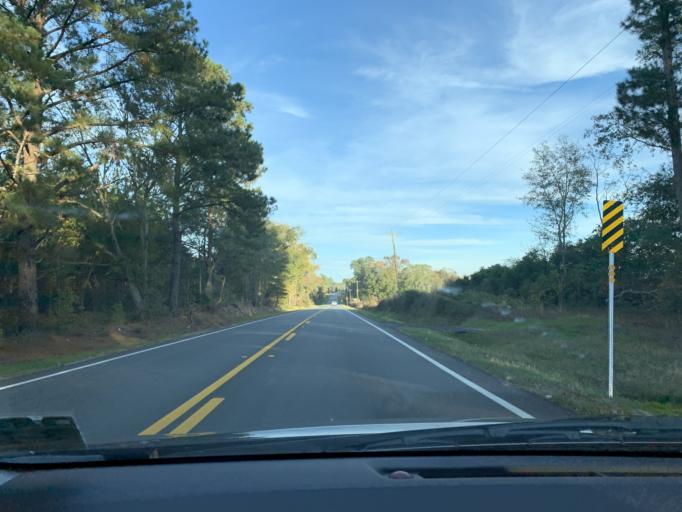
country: US
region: Georgia
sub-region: Irwin County
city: Ocilla
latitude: 31.5955
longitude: -83.1302
